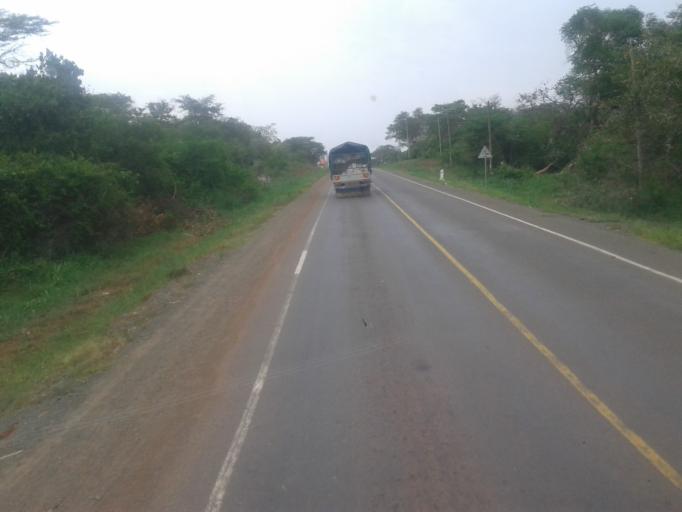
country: UG
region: Northern Region
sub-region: Oyam District
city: Oyam
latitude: 2.2523
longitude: 32.2371
